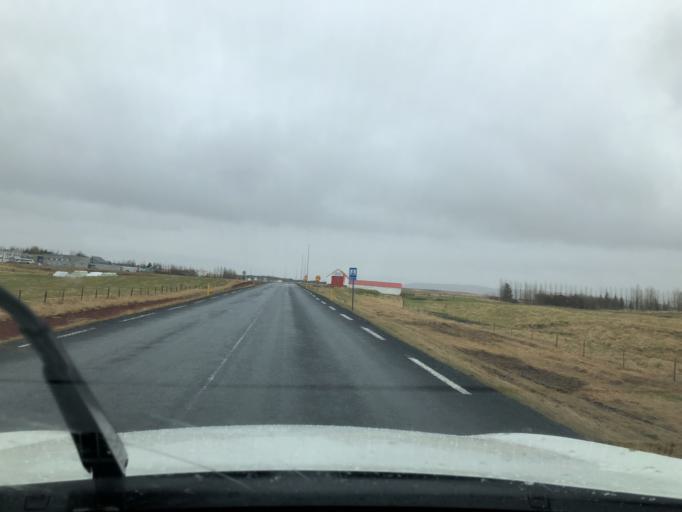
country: IS
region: South
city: Selfoss
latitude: 64.0721
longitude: -20.7747
